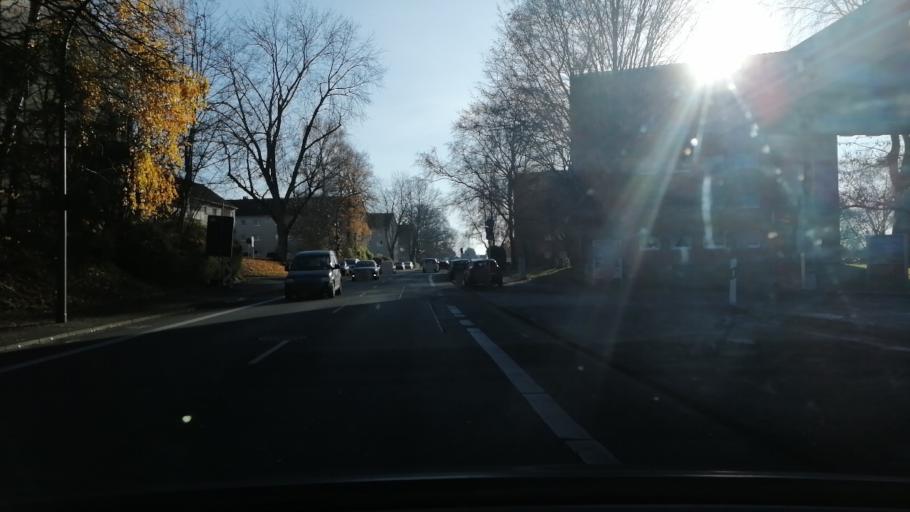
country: DE
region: North Rhine-Westphalia
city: Schwerte
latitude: 51.5055
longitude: 7.5581
